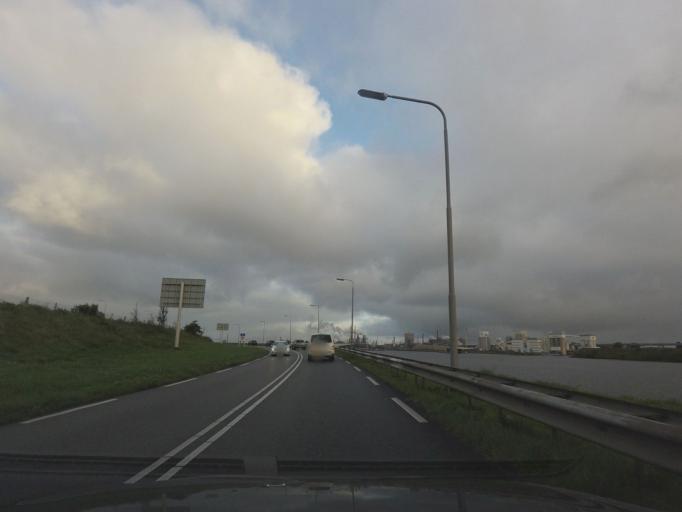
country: NL
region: North Holland
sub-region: Gemeente Velsen
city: Velsen-Zuid
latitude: 52.4633
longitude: 4.6299
